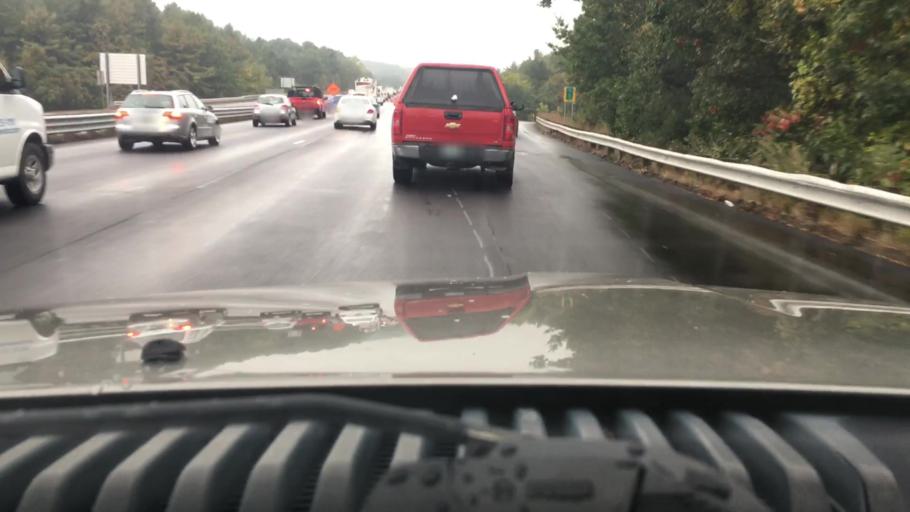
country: US
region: New Hampshire
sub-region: Hillsborough County
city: Manchester
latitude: 43.0141
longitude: -71.4797
